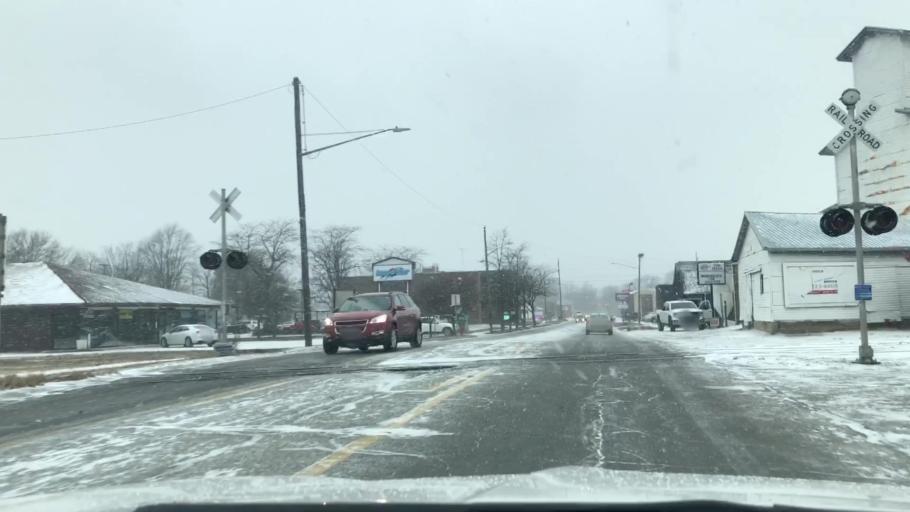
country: US
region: Indiana
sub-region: Fulton County
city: Rochester
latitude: 41.0648
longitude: -86.2110
